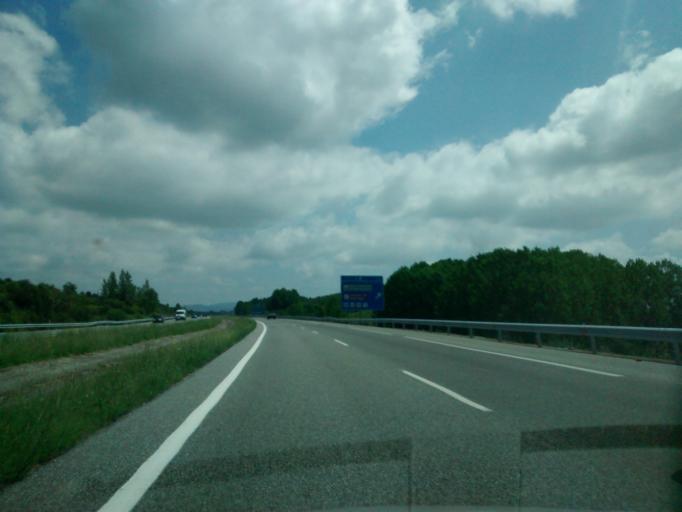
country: ES
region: Castille and Leon
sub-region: Provincia de Leon
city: Camponaraya
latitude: 42.5825
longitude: -6.6910
